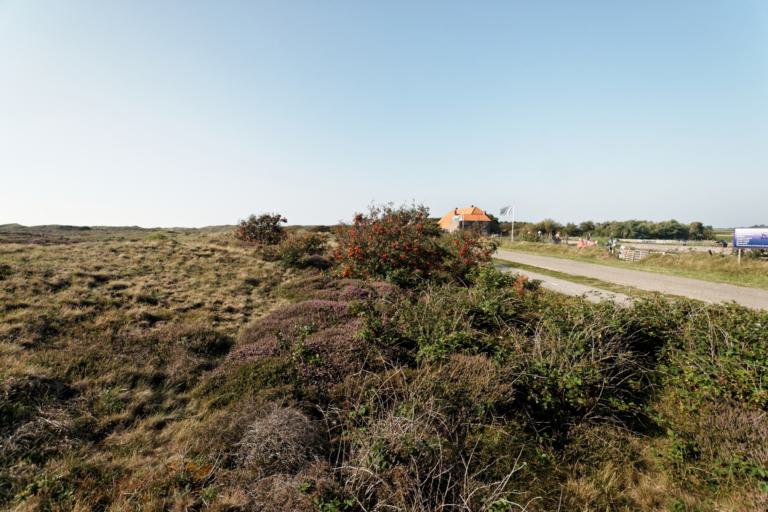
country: NL
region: North Holland
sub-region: Gemeente Texel
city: Den Burg
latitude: 53.0302
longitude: 4.7386
